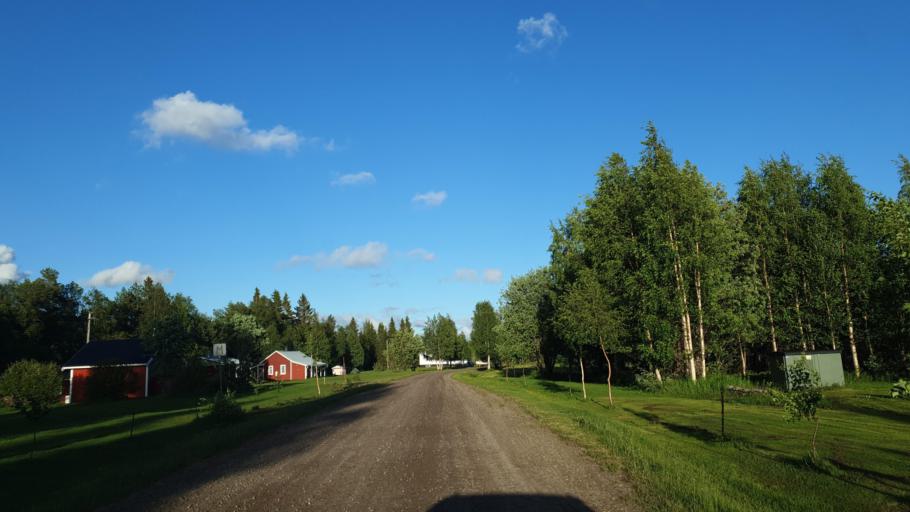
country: SE
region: Norrbotten
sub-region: Arvidsjaurs Kommun
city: Arvidsjaur
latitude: 65.7077
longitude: 18.7098
